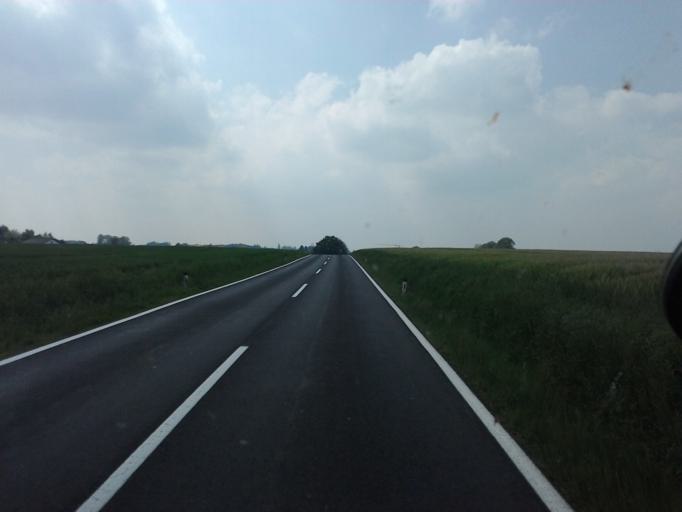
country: AT
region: Upper Austria
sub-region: Wels-Land
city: Sattledt
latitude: 48.0718
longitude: 14.0738
